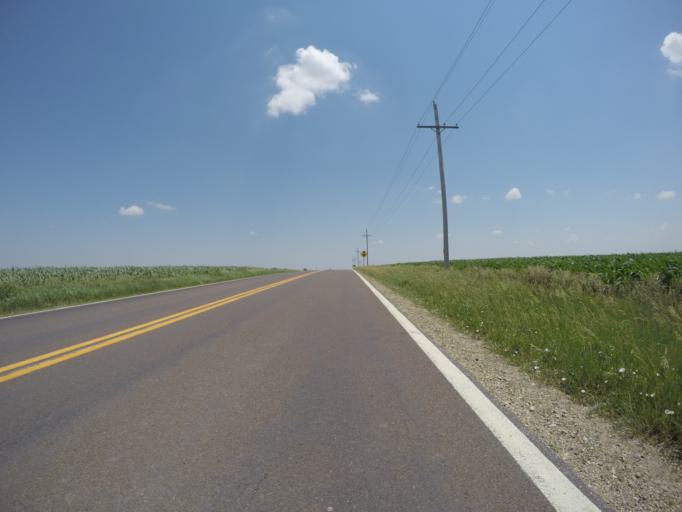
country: US
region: Kansas
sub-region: Doniphan County
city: Troy
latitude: 39.7399
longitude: -95.1485
